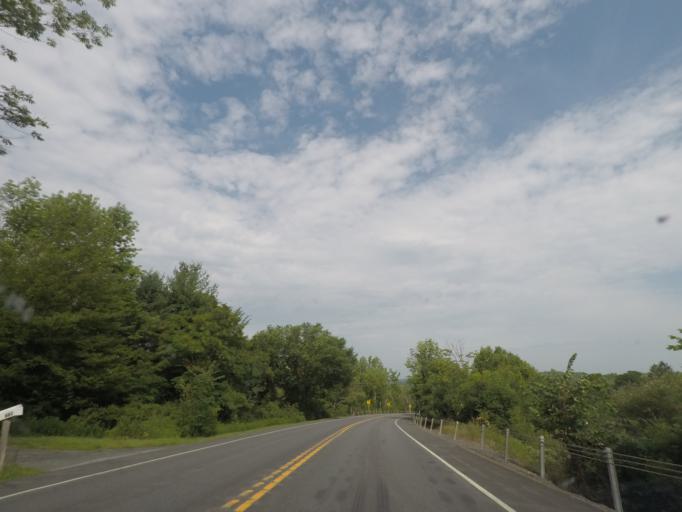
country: US
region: New York
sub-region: Rensselaer County
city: Poestenkill
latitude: 42.7316
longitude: -73.5611
